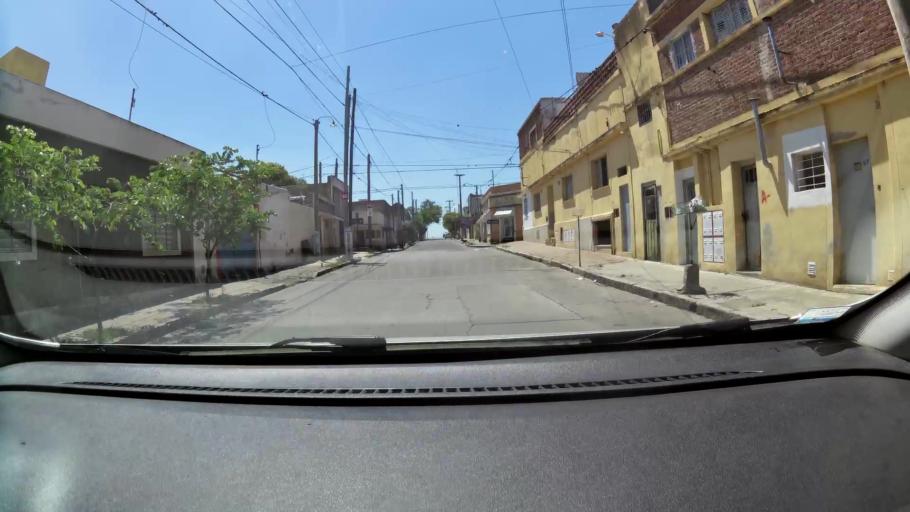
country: AR
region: Cordoba
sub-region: Departamento de Capital
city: Cordoba
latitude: -31.3959
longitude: -64.1985
